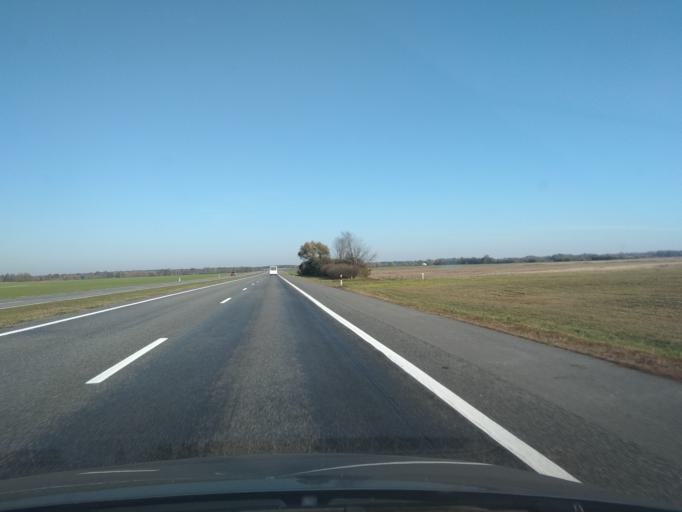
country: BY
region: Brest
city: Antopal'
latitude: 52.3211
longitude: 24.6179
